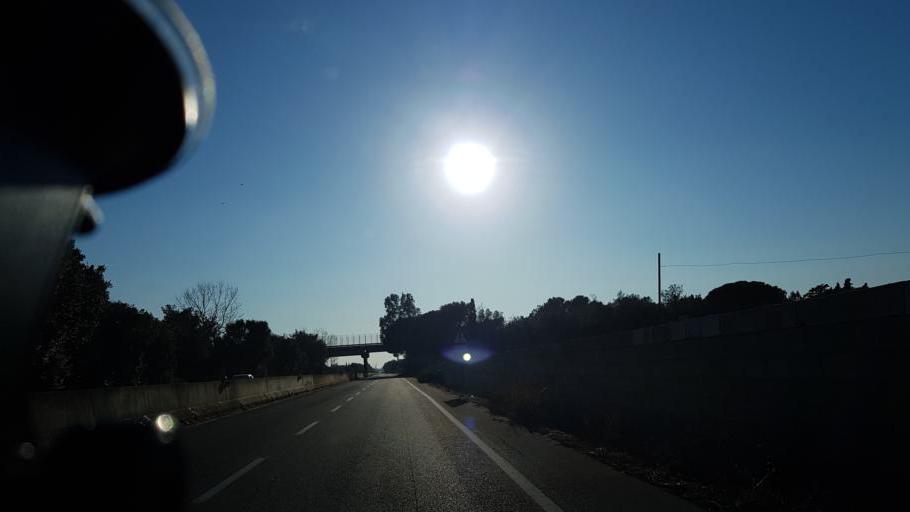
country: IT
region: Apulia
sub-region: Provincia di Lecce
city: Merine
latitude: 40.3741
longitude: 18.2459
